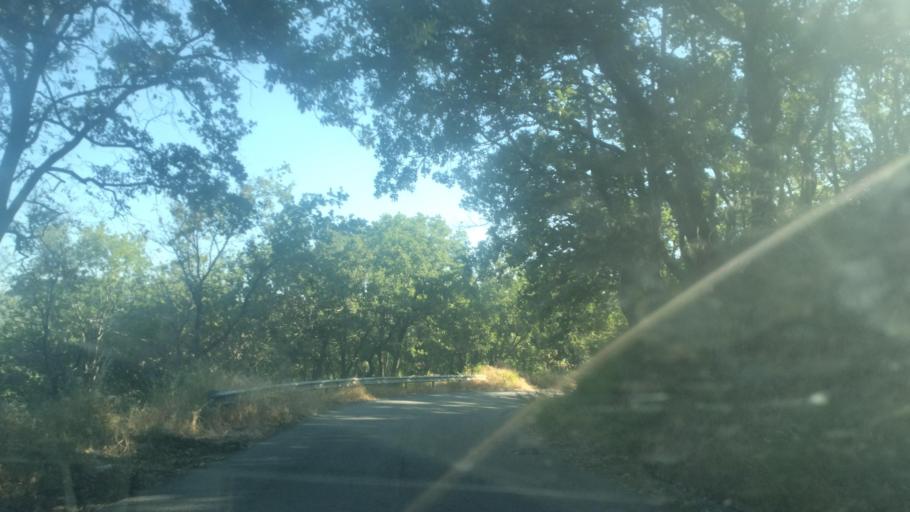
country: IT
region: Calabria
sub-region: Provincia di Catanzaro
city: Squillace
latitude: 38.7725
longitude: 16.5092
